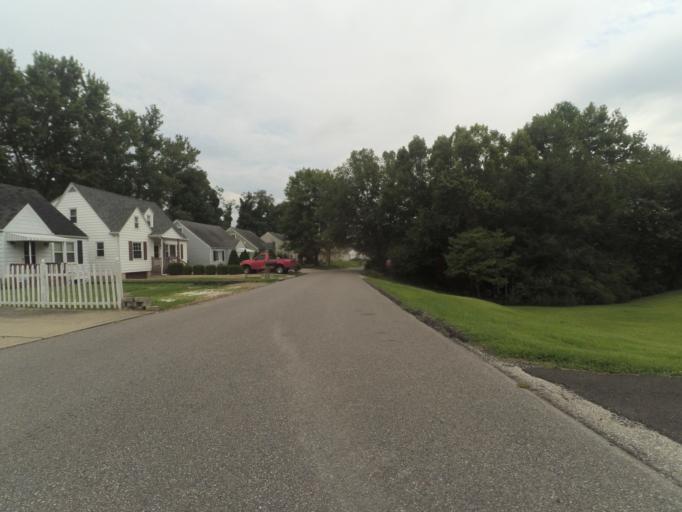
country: US
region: West Virginia
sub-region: Cabell County
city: Huntington
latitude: 38.3995
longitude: -82.4013
